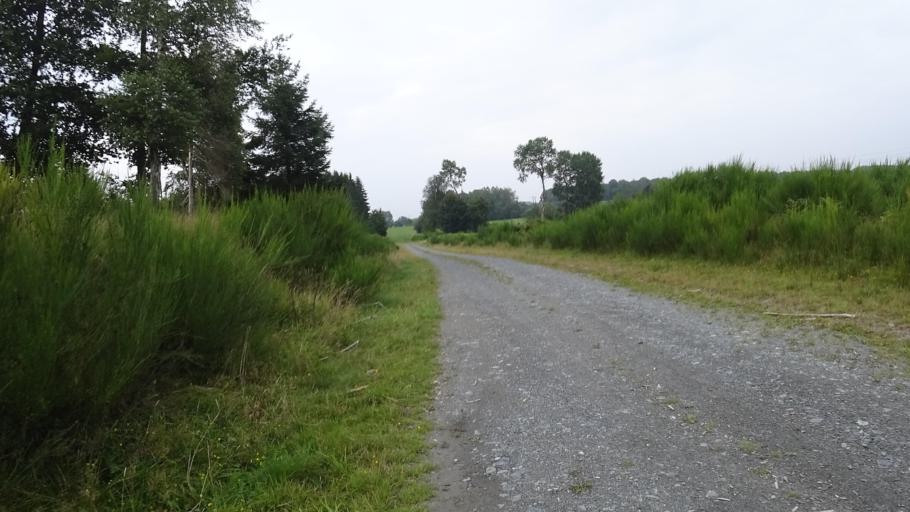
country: BE
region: Wallonia
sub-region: Province du Luxembourg
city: Chiny
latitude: 49.7925
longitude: 5.3275
